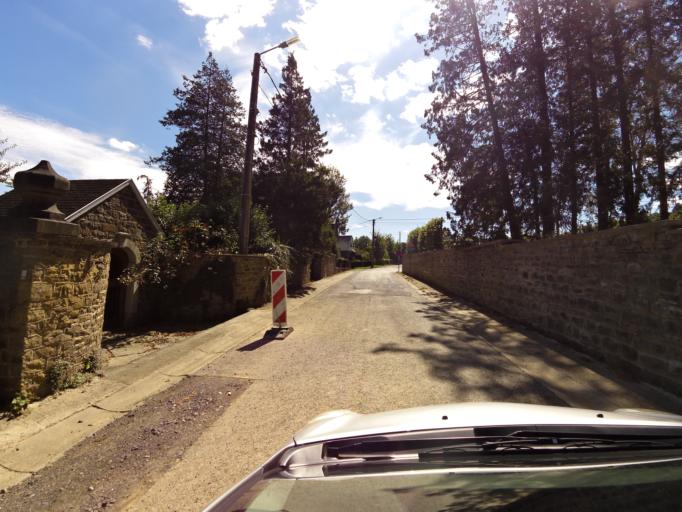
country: BE
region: Wallonia
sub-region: Province du Luxembourg
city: Rendeux
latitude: 50.2282
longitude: 5.5197
